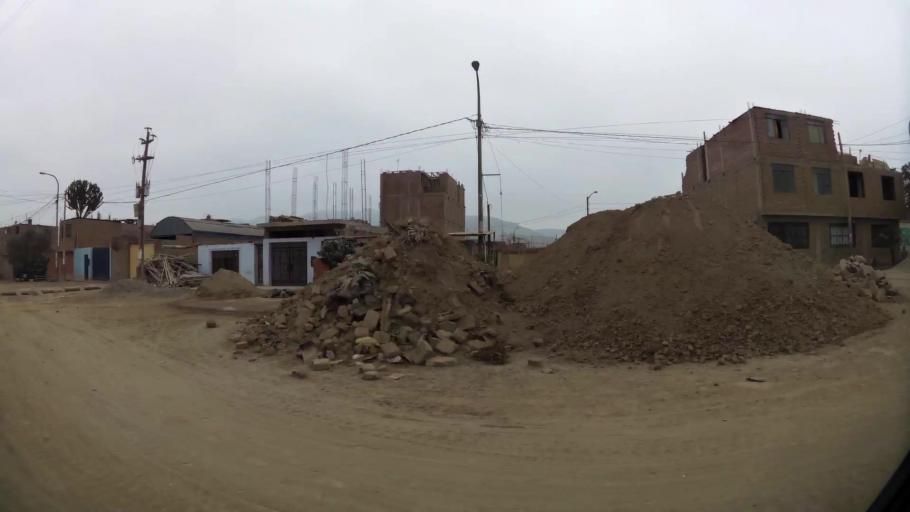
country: PE
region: Lima
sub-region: Lima
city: Urb. Santo Domingo
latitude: -11.8813
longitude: -77.0658
